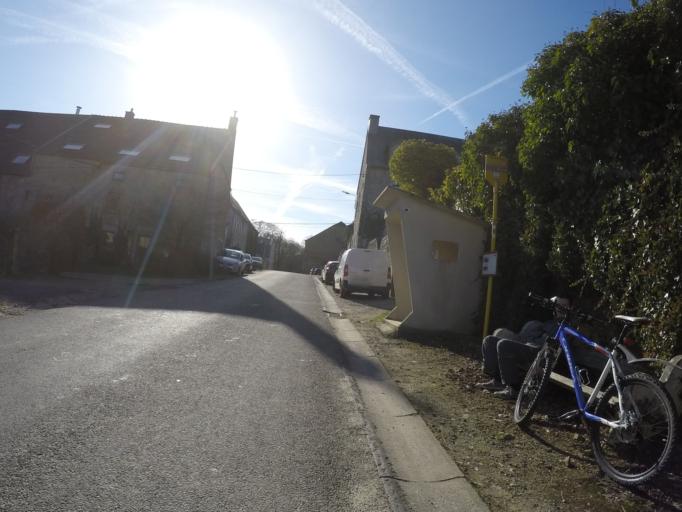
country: BE
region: Wallonia
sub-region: Province de Namur
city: Hamois
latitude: 50.3484
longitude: 5.1152
